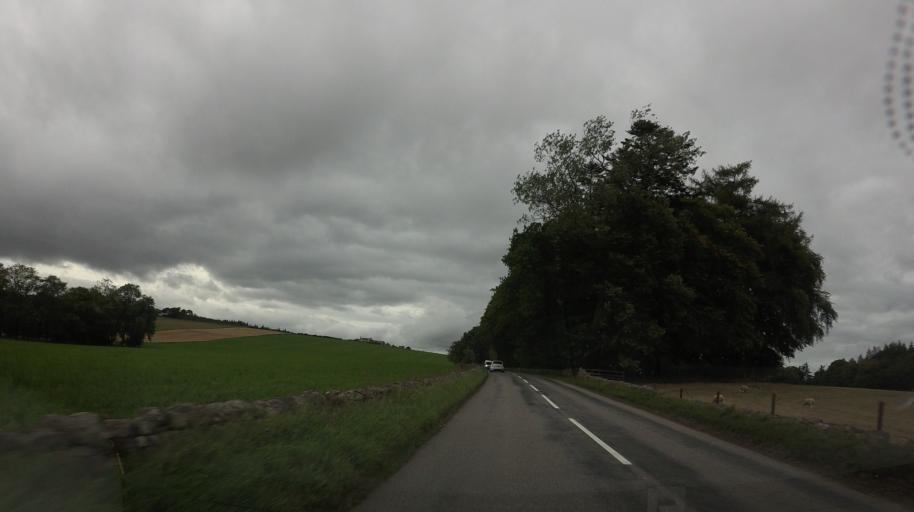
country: GB
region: Scotland
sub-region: Aberdeenshire
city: Kemnay
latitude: 57.1579
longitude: -2.4311
